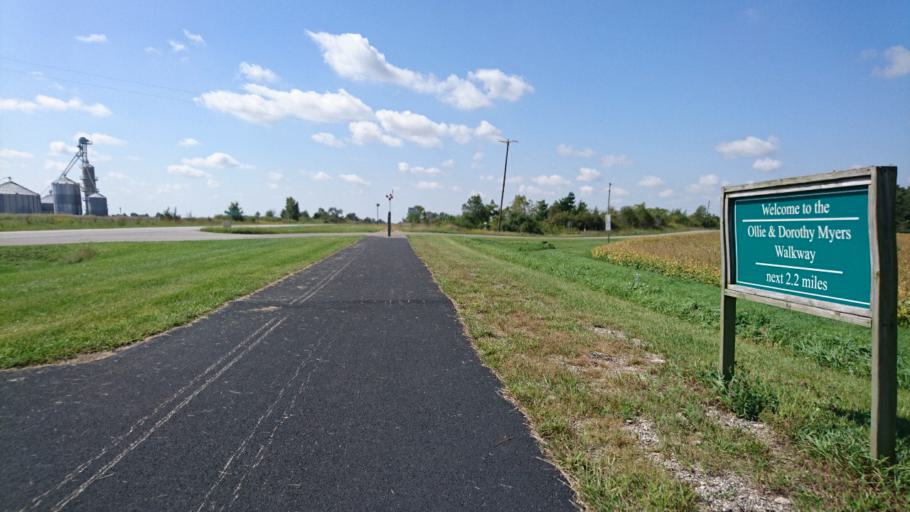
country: US
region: Illinois
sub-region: McLean County
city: Lexington
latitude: 40.6273
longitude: -88.8066
